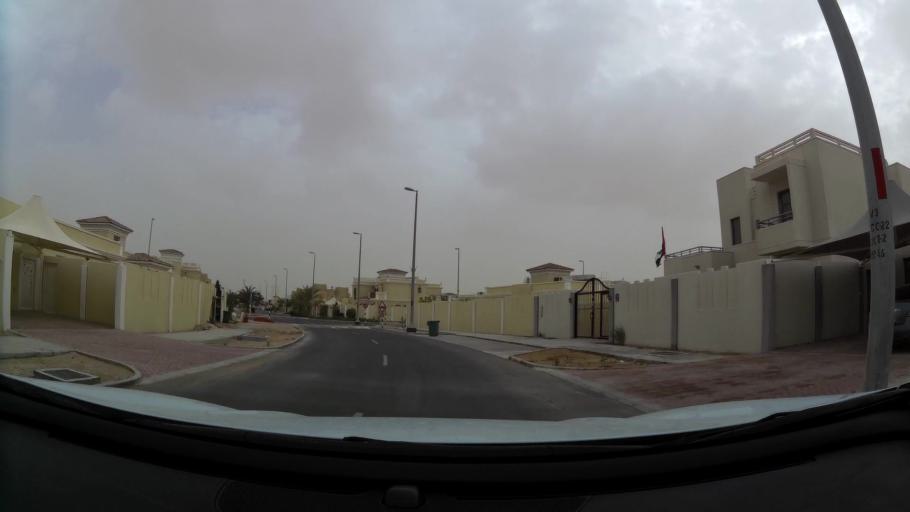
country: AE
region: Abu Dhabi
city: Abu Dhabi
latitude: 24.4540
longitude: 54.7392
